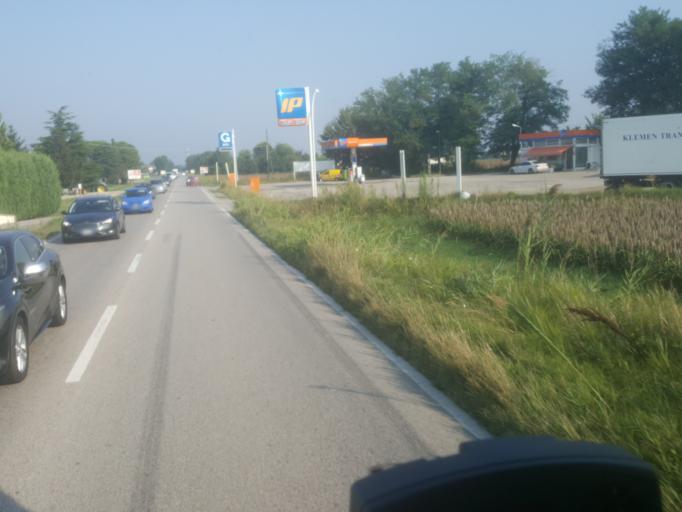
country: IT
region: Emilia-Romagna
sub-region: Provincia di Ravenna
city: Fornace Zarattini
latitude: 44.4388
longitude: 12.1405
